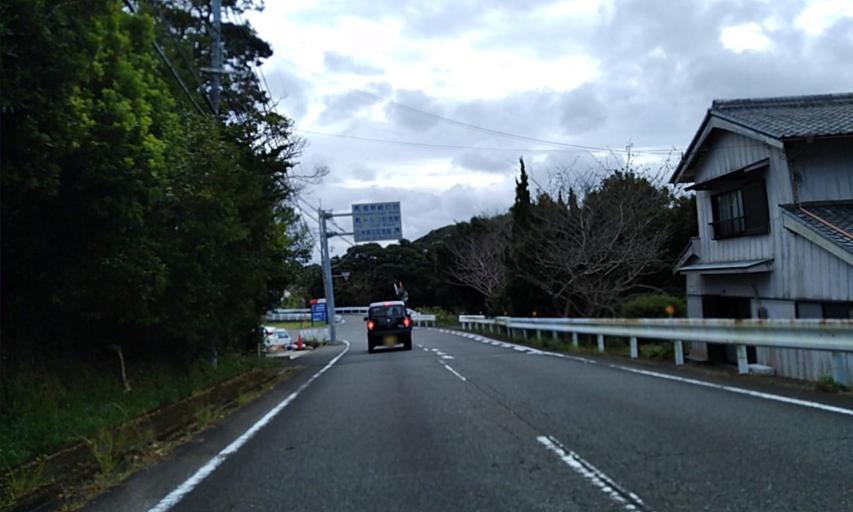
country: JP
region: Wakayama
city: Shingu
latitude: 33.4693
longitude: 135.8476
